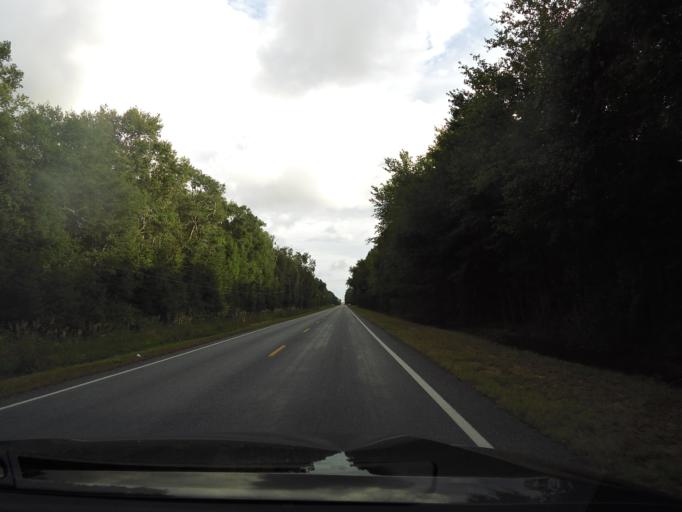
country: US
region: Georgia
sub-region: Liberty County
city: Midway
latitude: 31.6848
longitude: -81.4069
